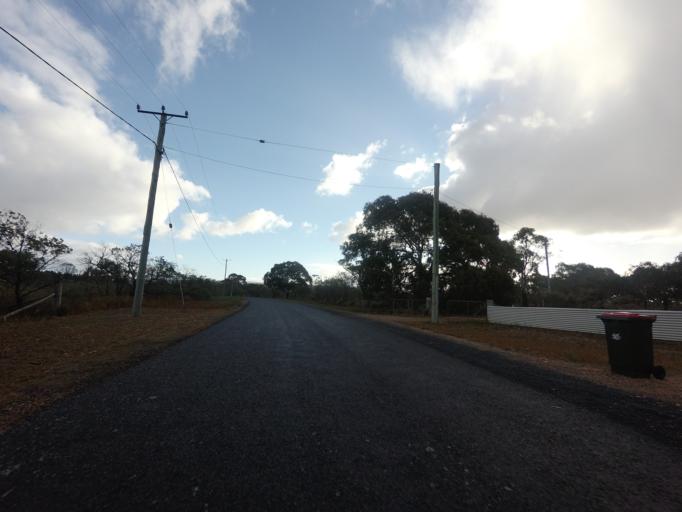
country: AU
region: Tasmania
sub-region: Break O'Day
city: St Helens
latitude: -42.1019
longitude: 148.0751
